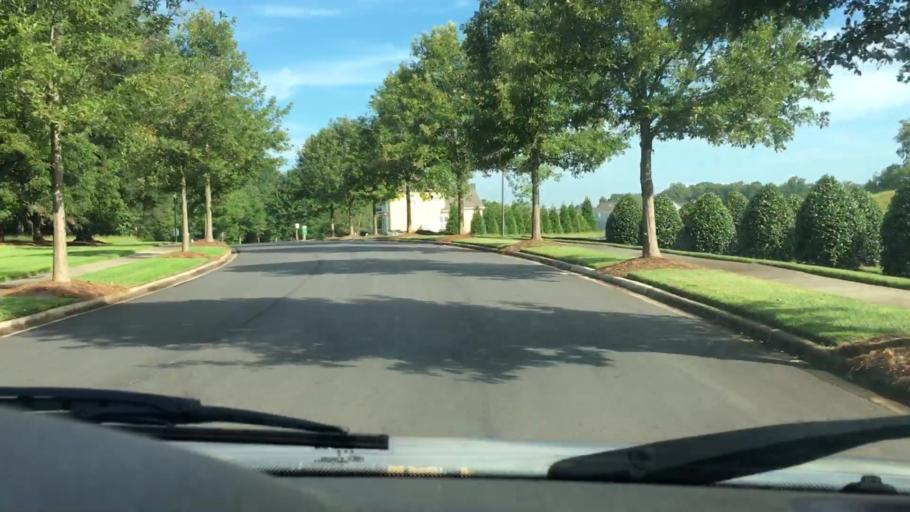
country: US
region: North Carolina
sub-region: Mecklenburg County
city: Huntersville
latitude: 35.4440
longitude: -80.7750
